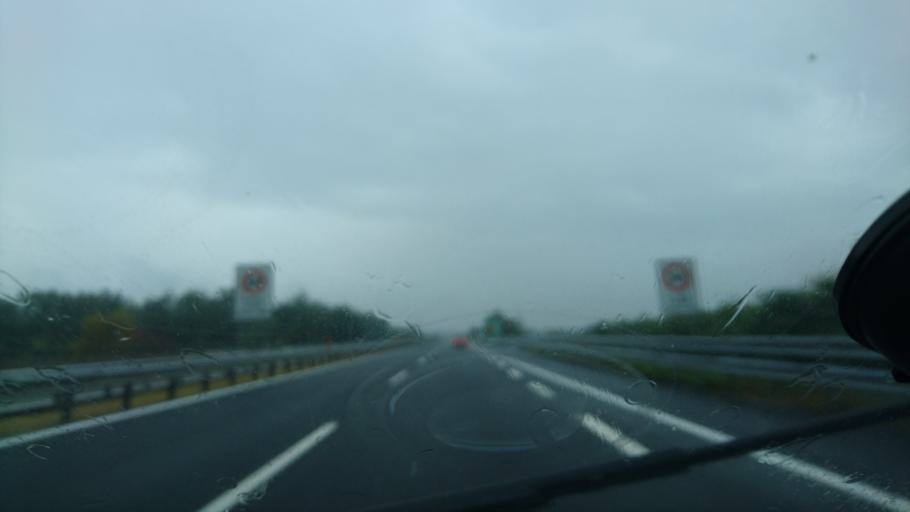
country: IT
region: Piedmont
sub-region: Provincia di Novara
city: Fontaneto D'Agogna
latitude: 45.6580
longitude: 8.4902
